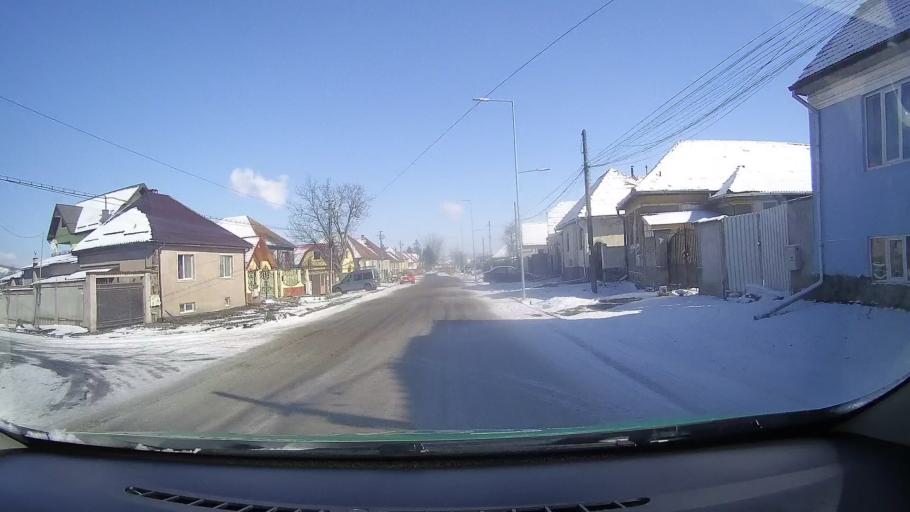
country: RO
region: Sibiu
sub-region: Comuna Avrig
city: Avrig
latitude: 45.7317
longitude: 24.3820
